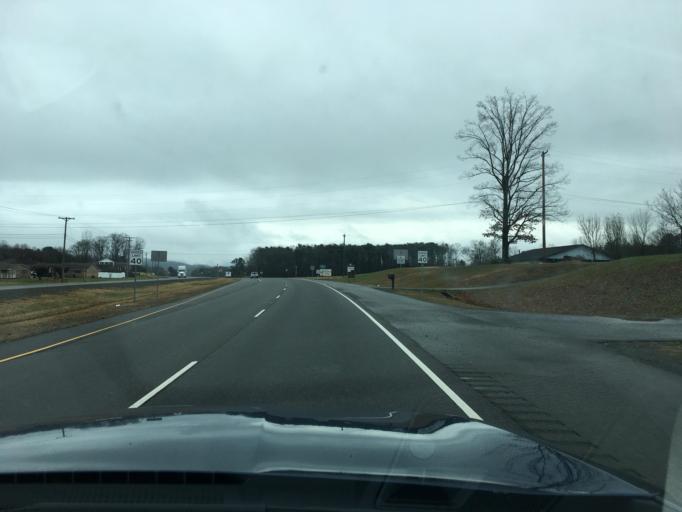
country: US
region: Tennessee
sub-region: McMinn County
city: Etowah
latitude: 35.3414
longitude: -84.5390
